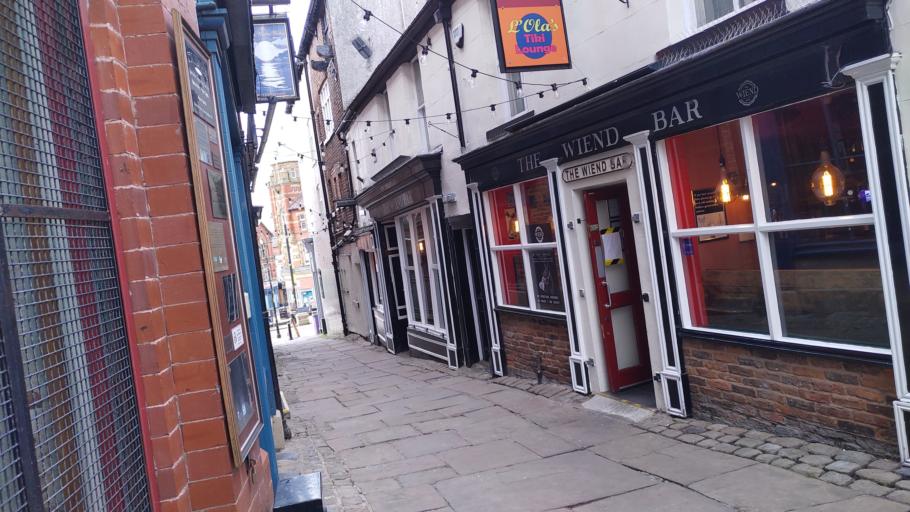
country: GB
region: England
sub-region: Borough of Wigan
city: Ince-in-Makerfield
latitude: 53.5459
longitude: -2.6310
